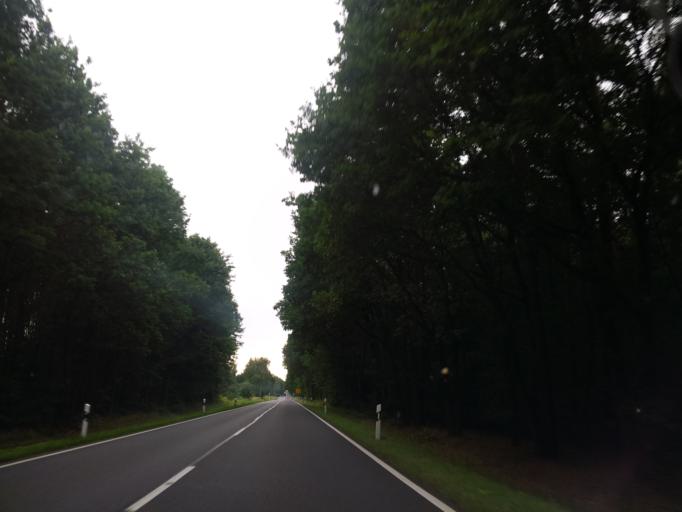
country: DE
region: Brandenburg
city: Treuenbrietzen
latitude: 52.0533
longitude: 12.9087
